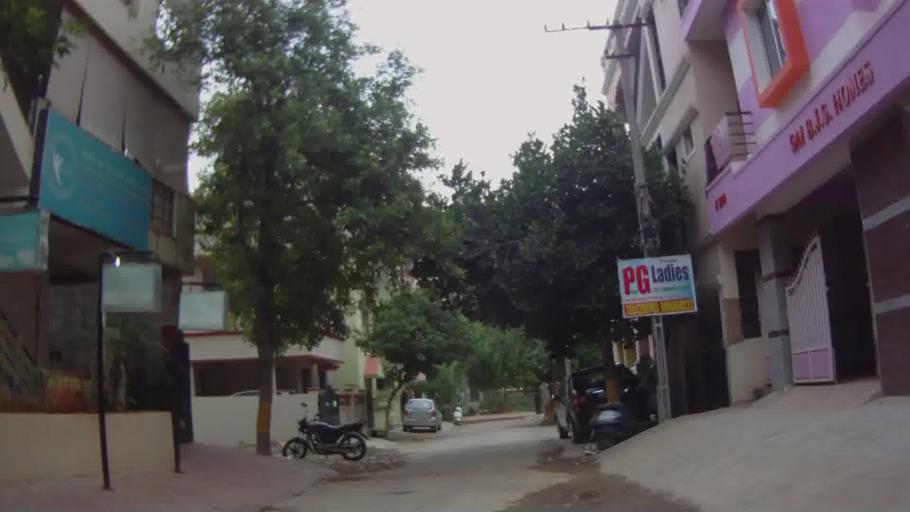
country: IN
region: Karnataka
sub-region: Bangalore Urban
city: Bangalore
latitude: 12.9601
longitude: 77.7179
